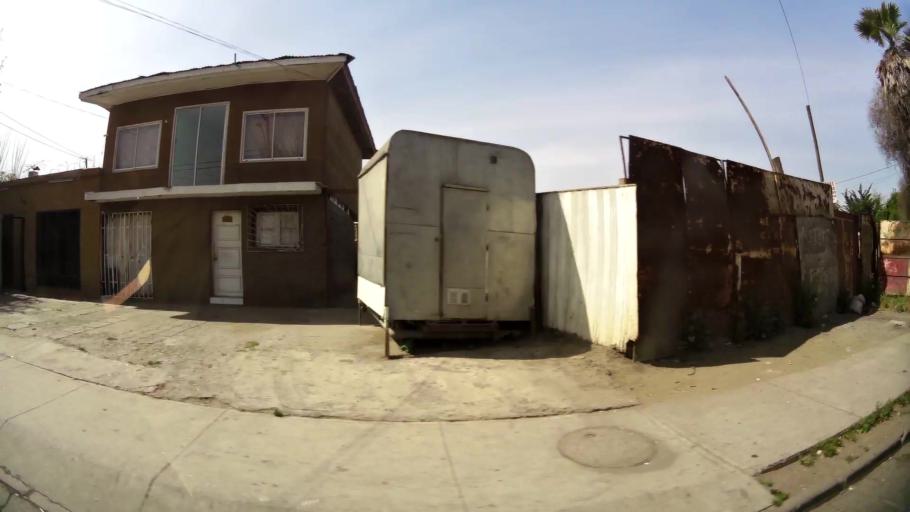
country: CL
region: Santiago Metropolitan
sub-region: Provincia de Santiago
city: Lo Prado
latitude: -33.4288
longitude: -70.7614
